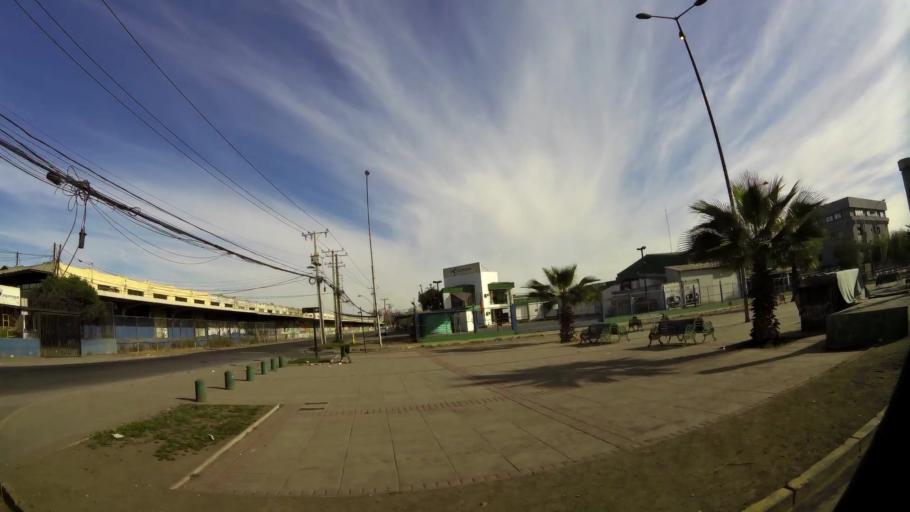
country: CL
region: Santiago Metropolitan
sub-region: Provincia de Santiago
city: Santiago
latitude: -33.4588
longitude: -70.6810
